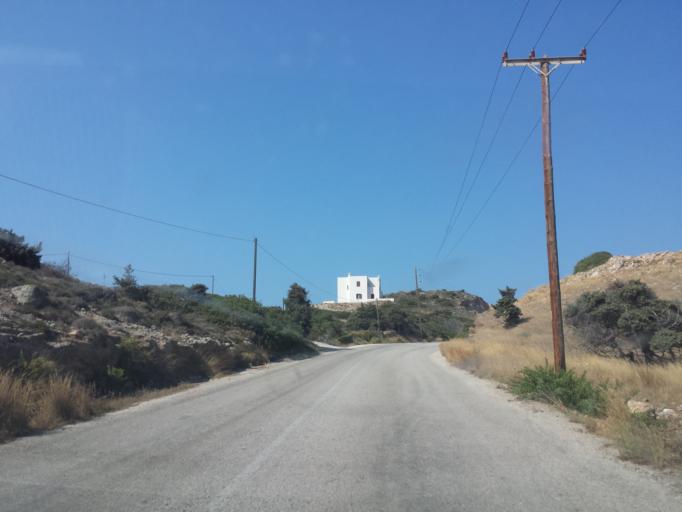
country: GR
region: South Aegean
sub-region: Nomos Kykladon
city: Adamas
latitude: 36.6947
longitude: 24.4610
